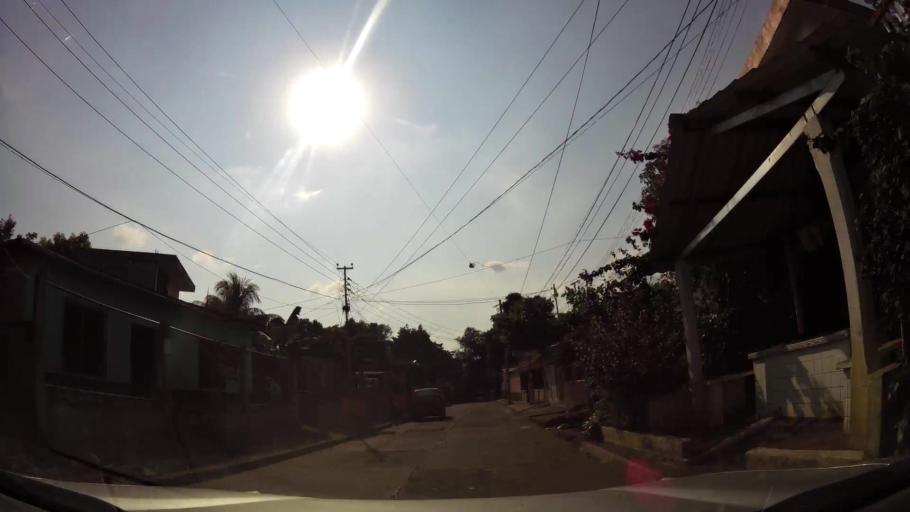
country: GT
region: Retalhuleu
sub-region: Municipio de Retalhuleu
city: Retalhuleu
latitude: 14.5368
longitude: -91.6922
